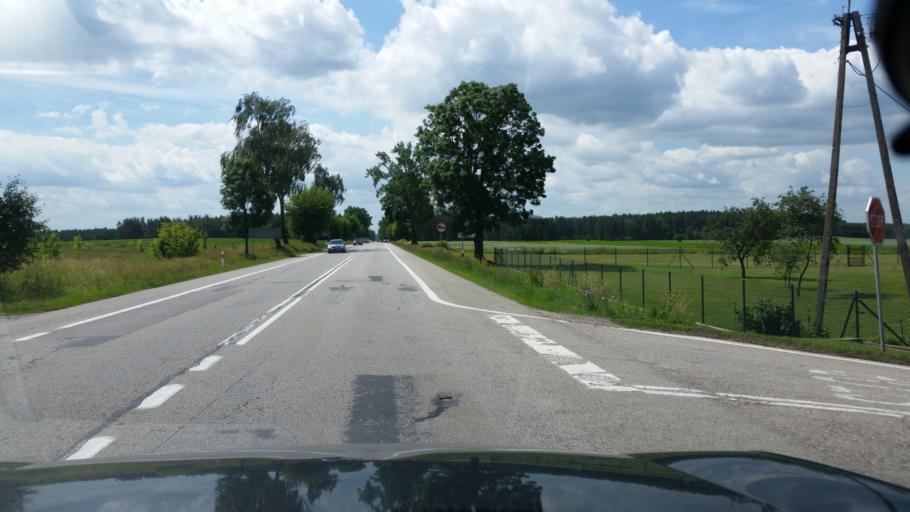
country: PL
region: Podlasie
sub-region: Powiat kolnenski
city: Stawiski
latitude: 53.2928
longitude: 22.1453
